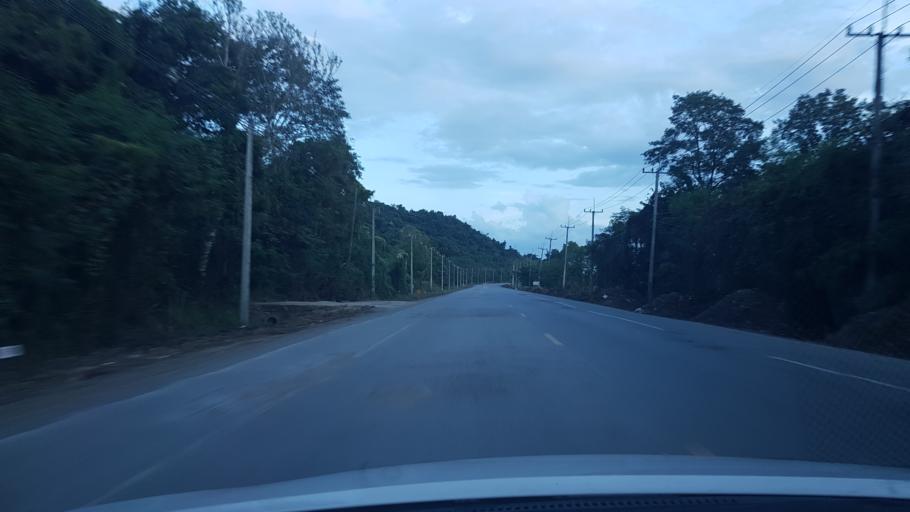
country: TH
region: Sara Buri
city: Kaeng Khoi
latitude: 14.4847
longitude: 101.0485
